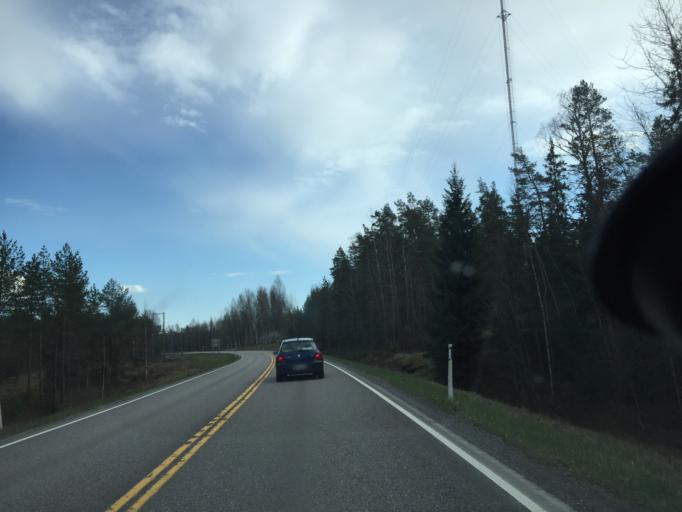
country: FI
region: Uusimaa
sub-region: Raaseporin
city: Ekenaes
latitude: 60.0199
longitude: 23.3779
